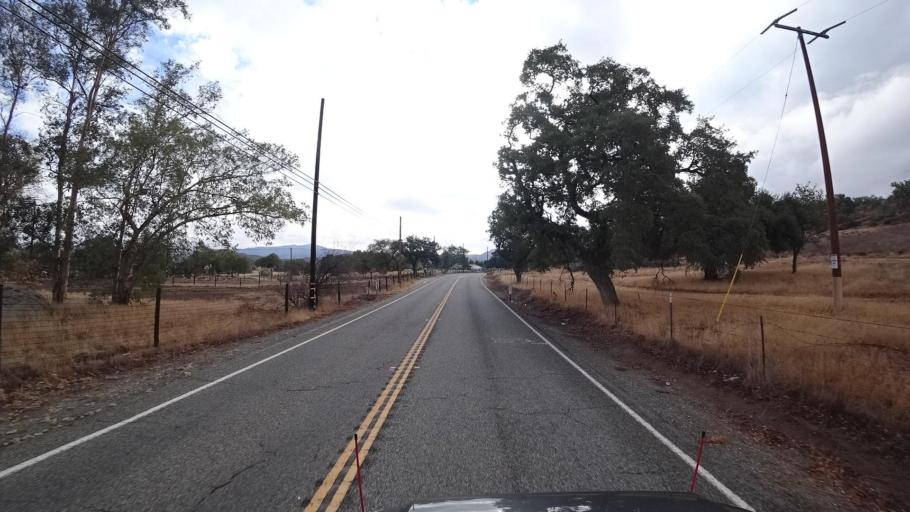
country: MX
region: Baja California
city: Tecate
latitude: 32.6076
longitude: -116.6230
